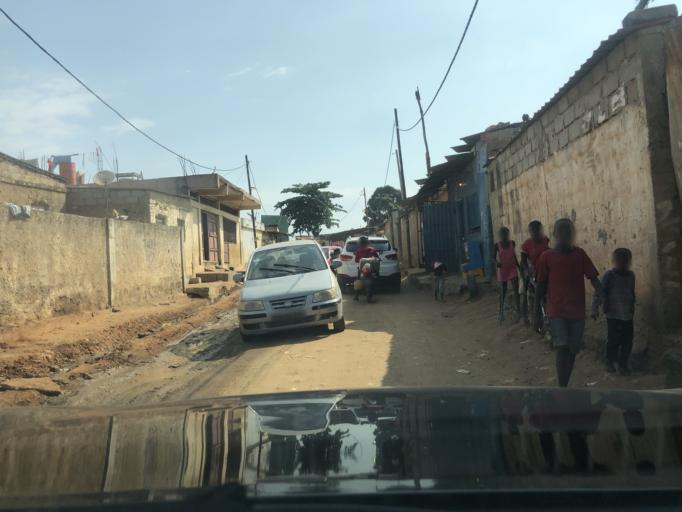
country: AO
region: Luanda
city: Luanda
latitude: -8.8524
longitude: 13.2559
